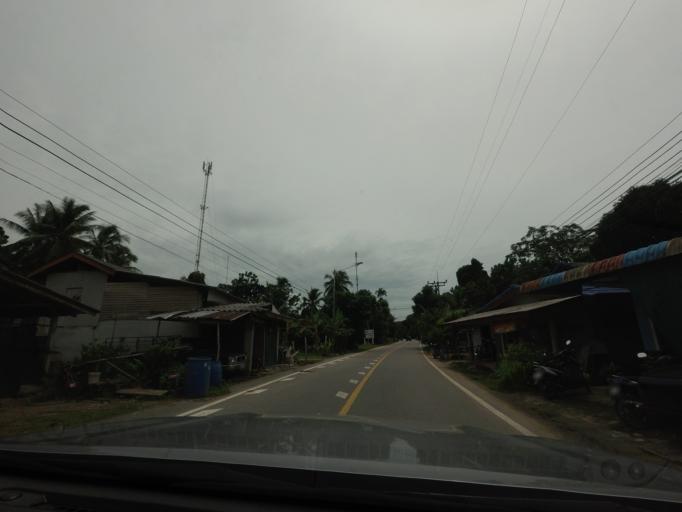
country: TH
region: Pattani
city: Kapho
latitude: 6.5950
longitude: 101.5303
